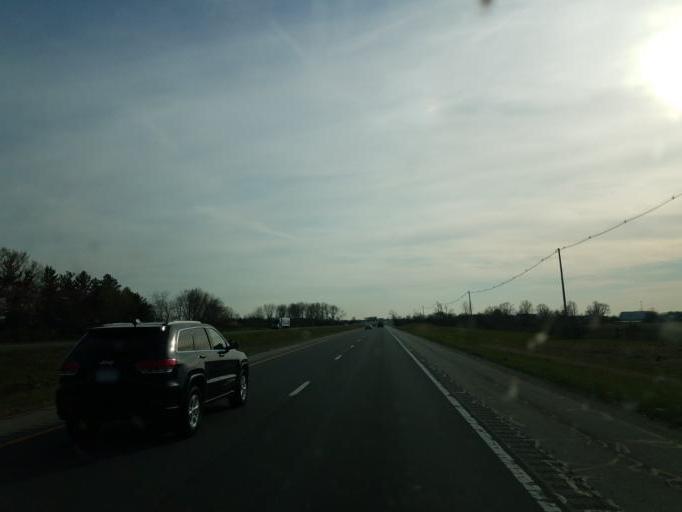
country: US
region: Ohio
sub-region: Fayette County
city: Jeffersonville
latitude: 39.6701
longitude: -83.5044
